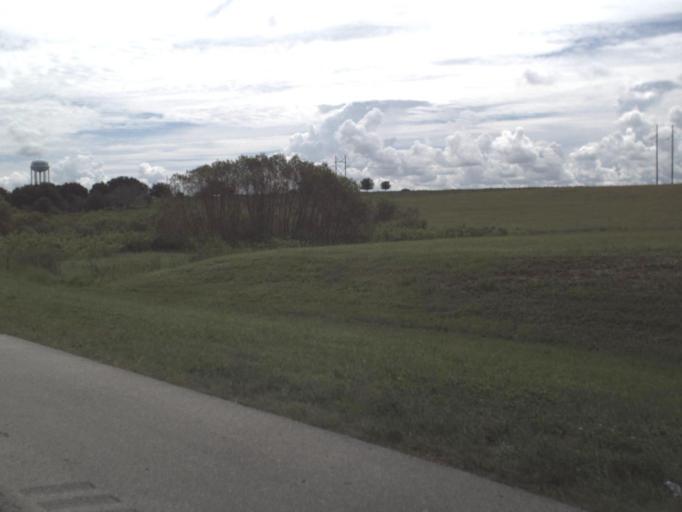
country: US
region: Florida
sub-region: Polk County
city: Polk City
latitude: 28.1574
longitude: -81.8125
